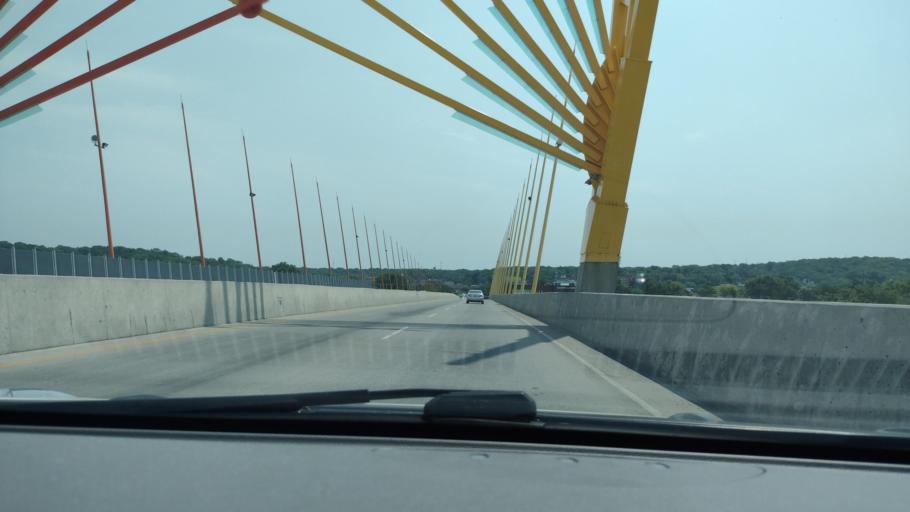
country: US
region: Iowa
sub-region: Pottawattamie County
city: Council Bluffs
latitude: 41.2618
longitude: -95.8620
